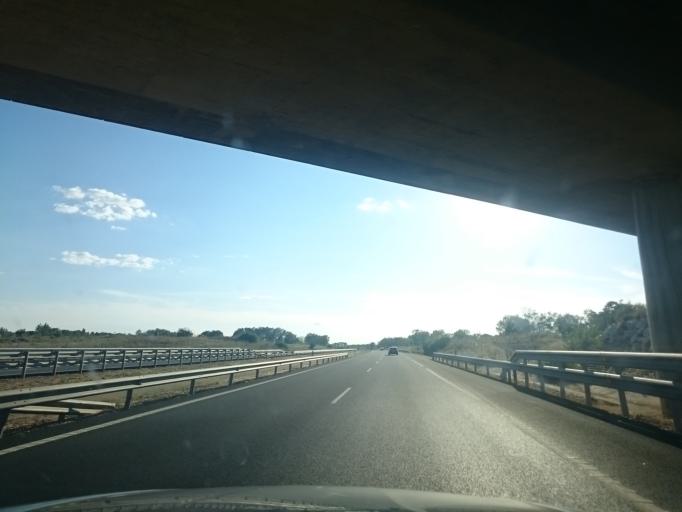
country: ES
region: Castille and Leon
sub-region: Provincia de Burgos
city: Melgar de Fernamental
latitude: 42.4086
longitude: -4.2810
